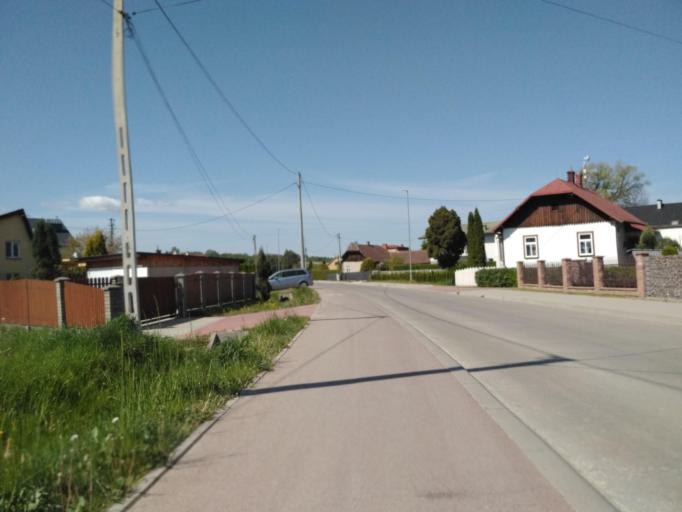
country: PL
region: Subcarpathian Voivodeship
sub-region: Powiat krosnienski
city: Korczyna
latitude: 49.6980
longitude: 21.8058
